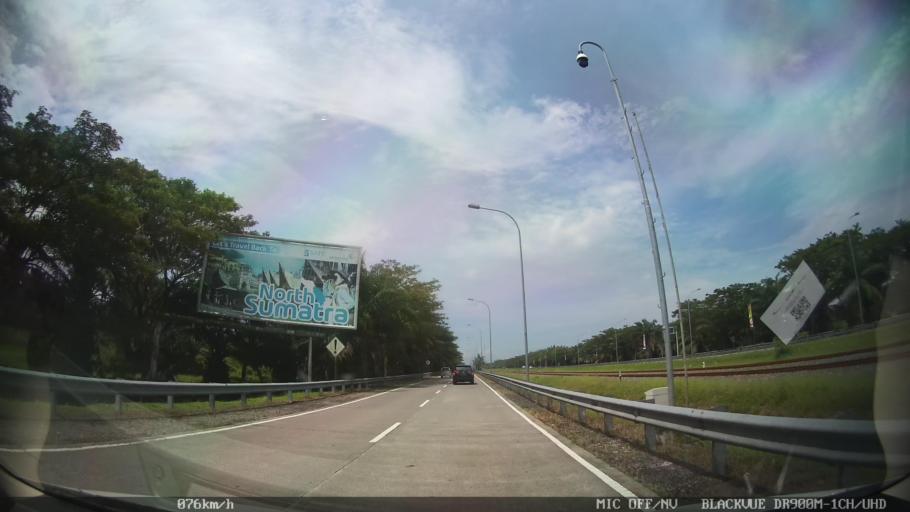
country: ID
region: North Sumatra
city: Percut
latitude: 3.6278
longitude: 98.8716
